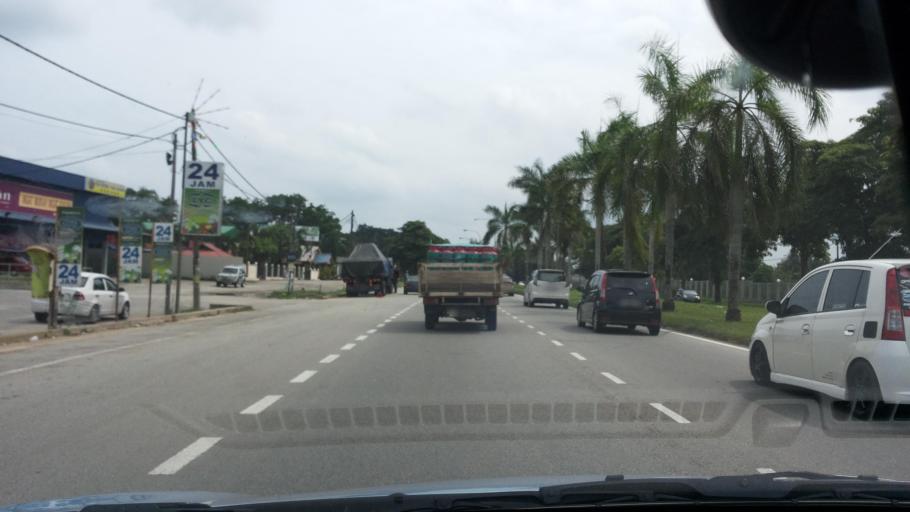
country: MY
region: Pahang
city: Kuantan
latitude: 3.7648
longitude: 103.2181
